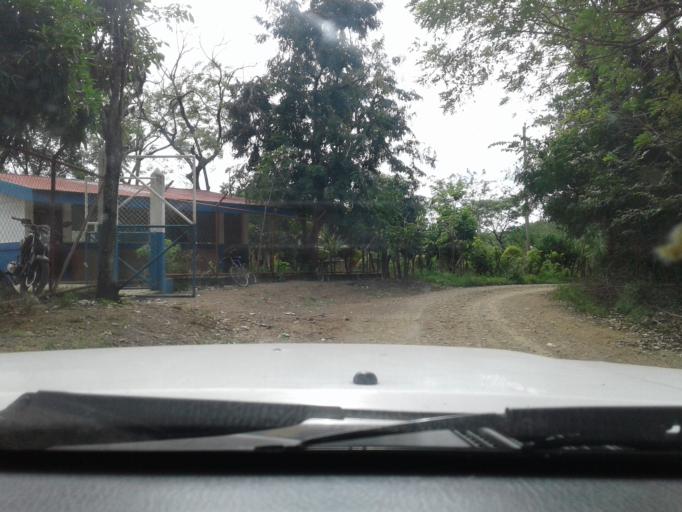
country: NI
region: Rivas
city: San Juan del Sur
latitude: 11.2139
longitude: -85.7942
